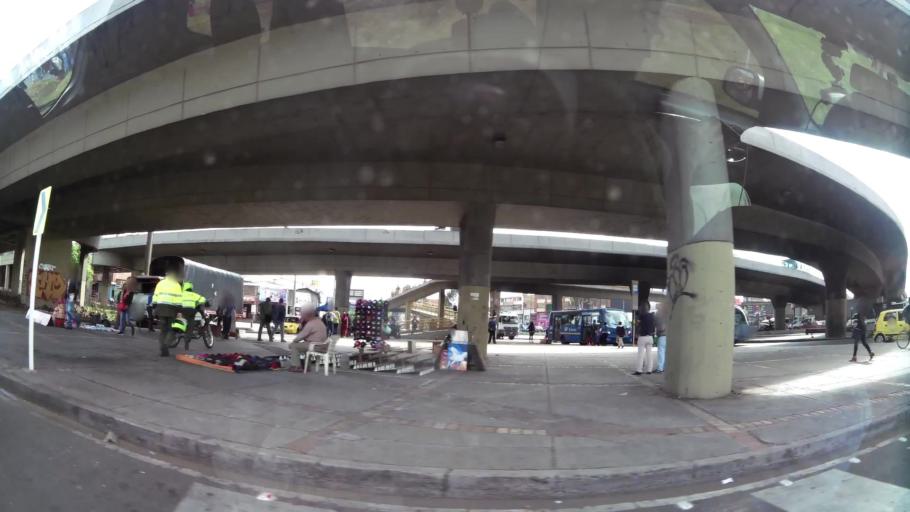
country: CO
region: Bogota D.C.
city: Bogota
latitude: 4.6187
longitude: -74.1391
